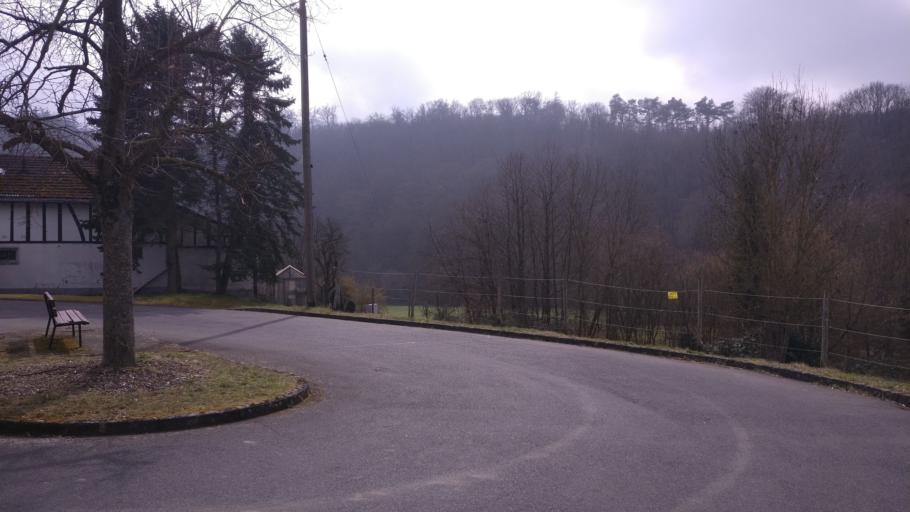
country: DE
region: Rheinland-Pfalz
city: Rossbach
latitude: 50.6193
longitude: 7.4221
